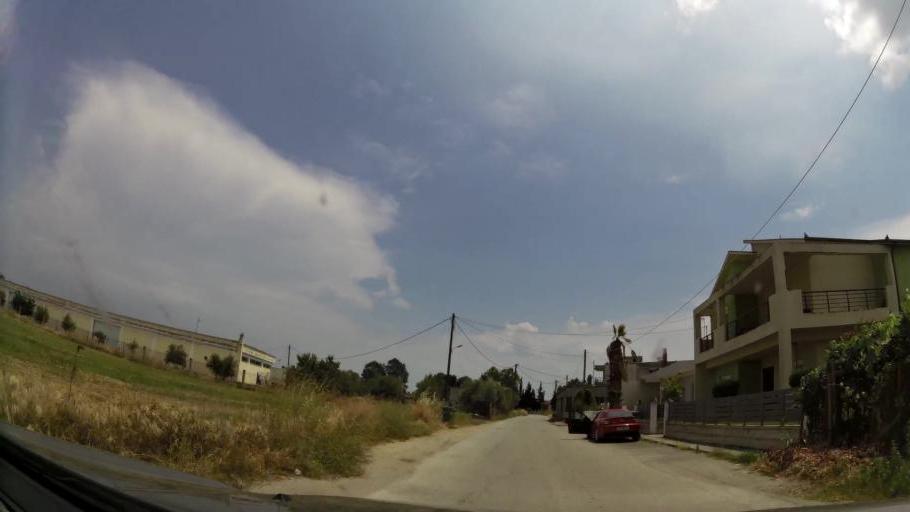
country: GR
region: Central Macedonia
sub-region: Nomos Pierias
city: Peristasi
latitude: 40.2720
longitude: 22.5467
